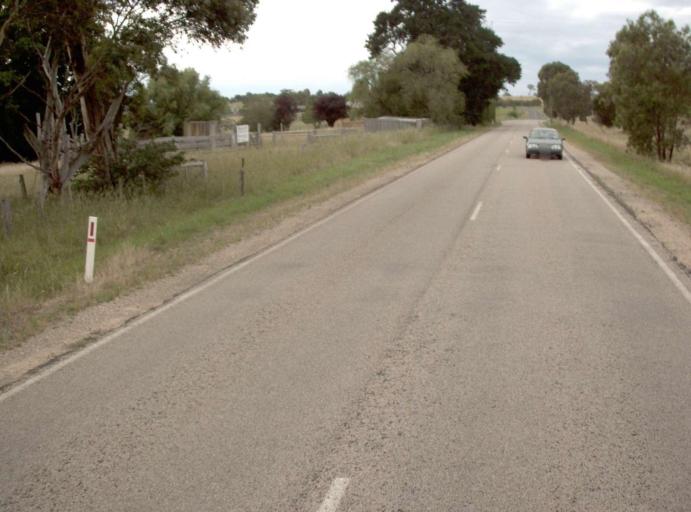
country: AU
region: Victoria
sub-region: East Gippsland
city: Bairnsdale
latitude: -37.8136
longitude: 147.4891
